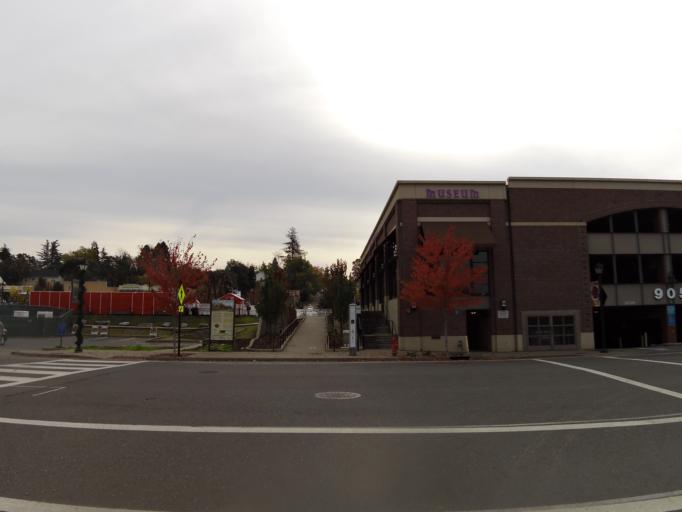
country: US
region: California
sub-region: Sacramento County
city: Folsom
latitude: 38.6772
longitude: -121.1799
